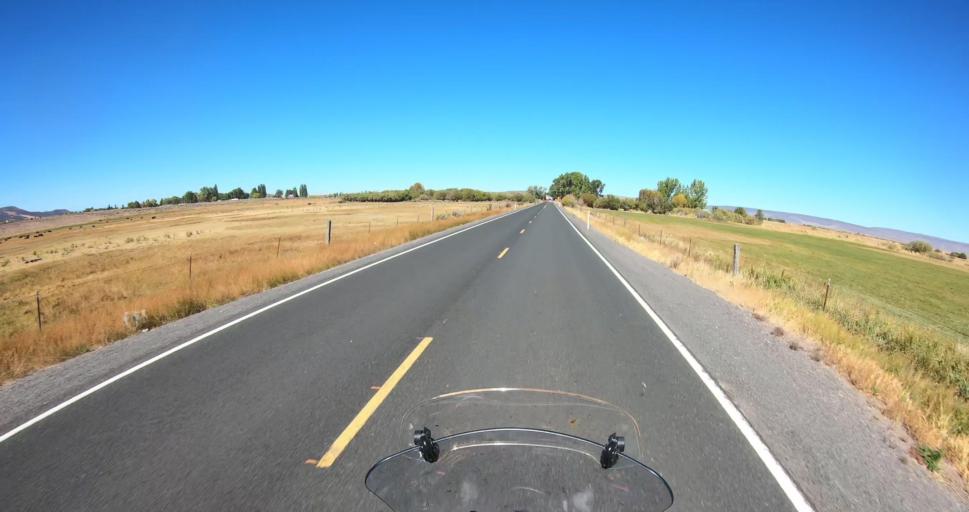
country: US
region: Oregon
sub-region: Lake County
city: Lakeview
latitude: 42.6804
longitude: -120.5283
